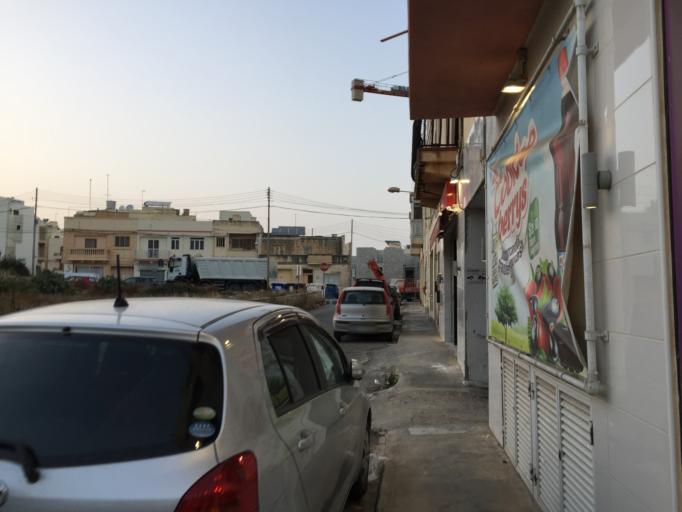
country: MT
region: Haz-Zabbar
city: Zabbar
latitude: 35.8713
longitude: 14.5349
